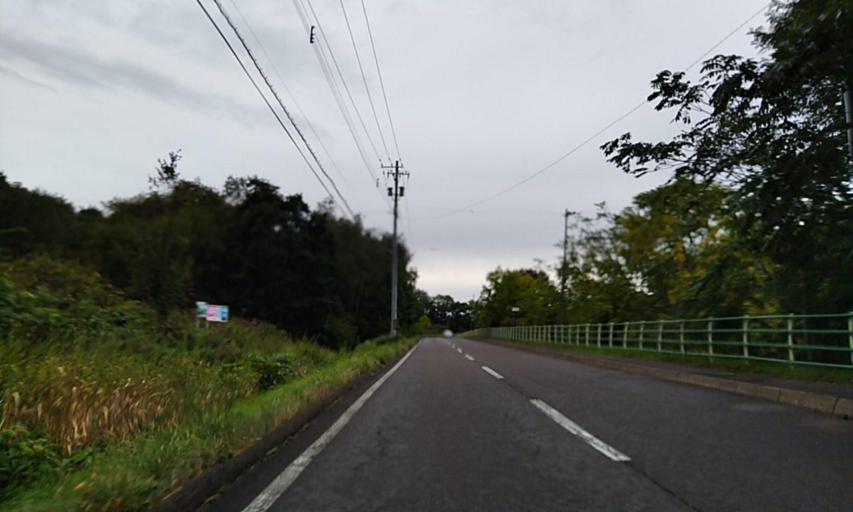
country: JP
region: Hokkaido
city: Abashiri
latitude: 43.9999
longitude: 144.2293
